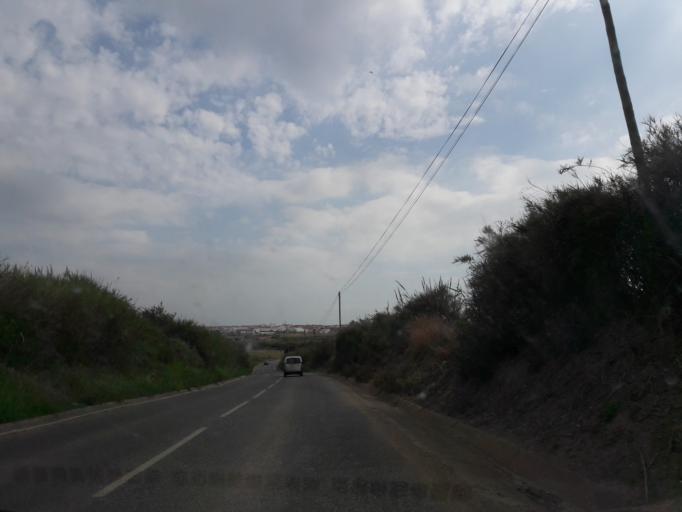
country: PT
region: Leiria
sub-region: Peniche
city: Atouguia da Baleia
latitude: 39.3494
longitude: -9.3236
